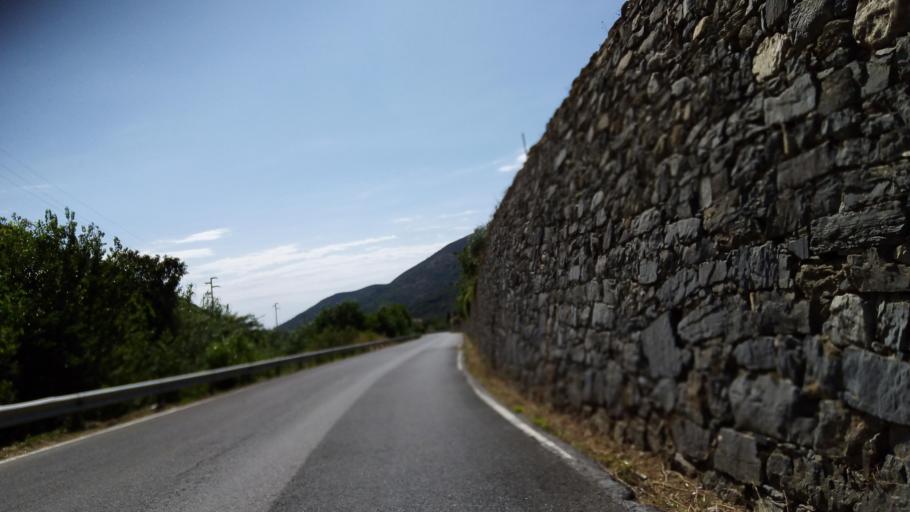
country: IT
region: Liguria
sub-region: Provincia di Savona
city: Toirano
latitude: 44.1339
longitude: 8.1999
